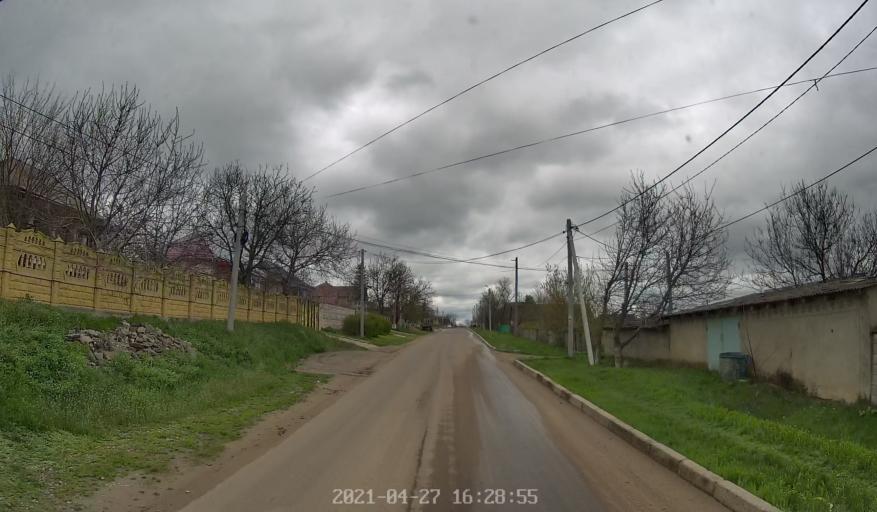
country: MD
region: Chisinau
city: Singera
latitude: 46.9697
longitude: 29.0464
